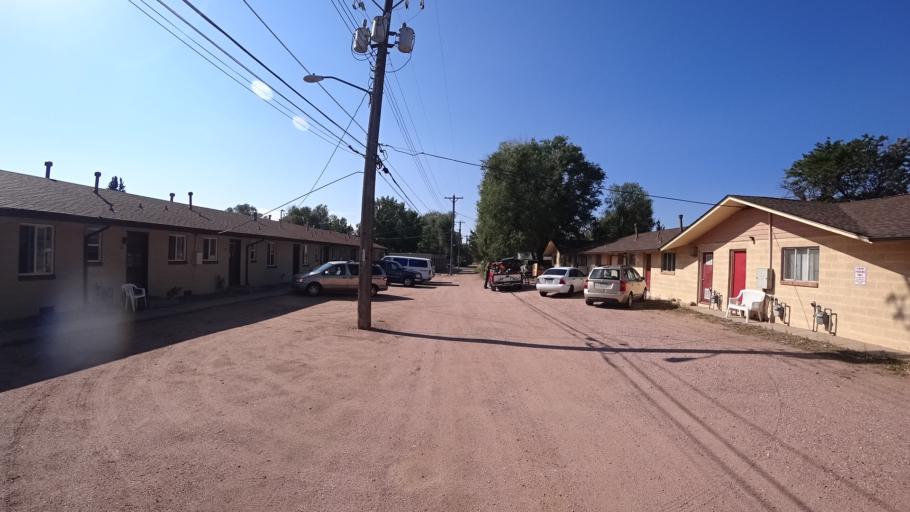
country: US
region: Colorado
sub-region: El Paso County
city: Colorado Springs
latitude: 38.8745
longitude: -104.8249
